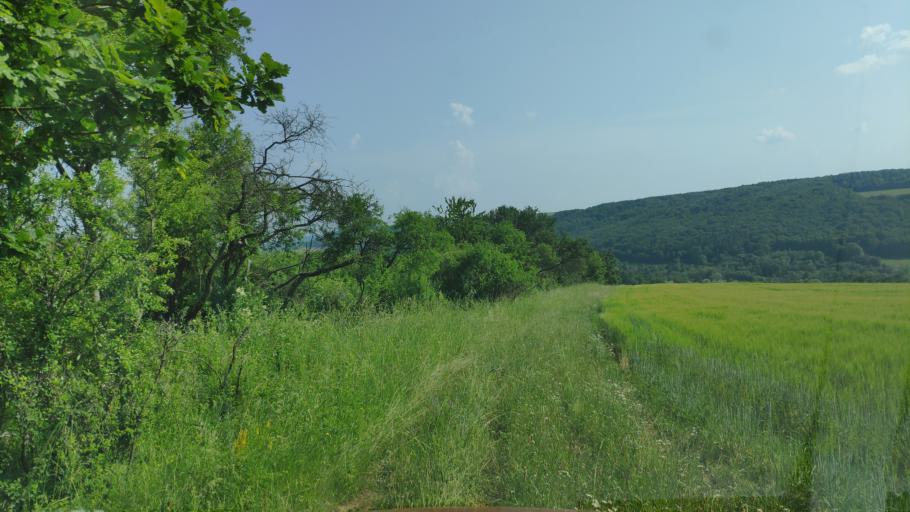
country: SK
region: Presovsky
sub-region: Okres Presov
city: Presov
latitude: 48.9618
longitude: 21.1545
